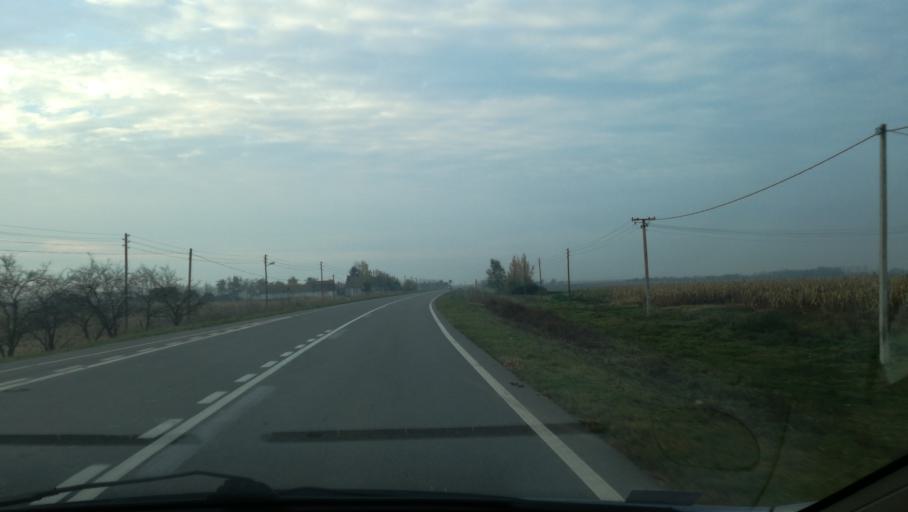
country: RS
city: Banatska Topola
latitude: 45.6854
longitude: 20.4234
